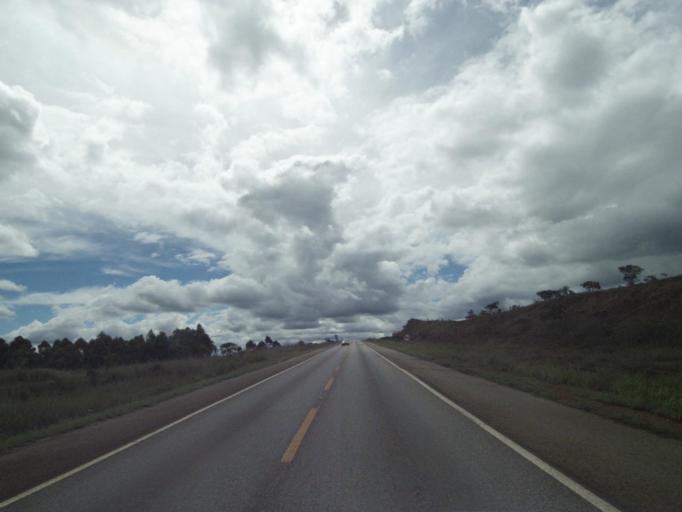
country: BR
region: Goias
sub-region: Pirenopolis
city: Pirenopolis
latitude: -15.7644
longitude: -48.7275
